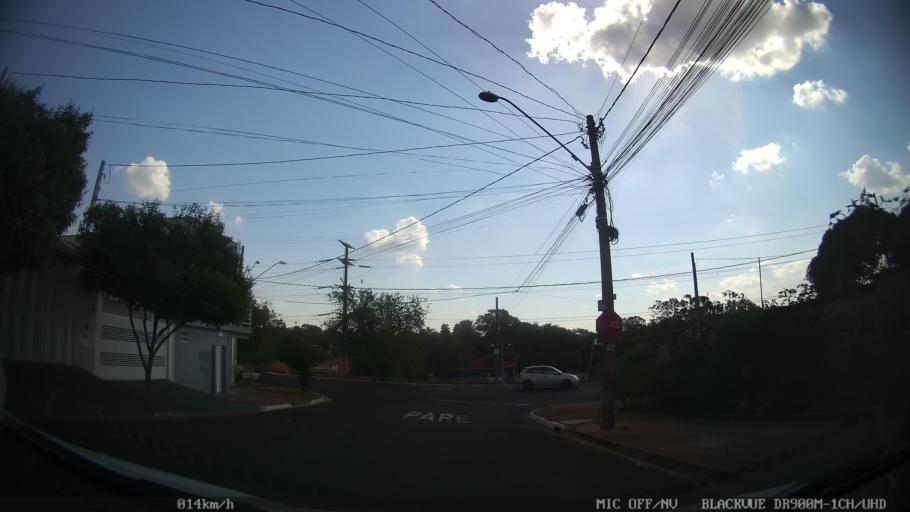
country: BR
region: Sao Paulo
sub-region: Ribeirao Preto
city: Ribeirao Preto
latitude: -21.1808
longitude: -47.8396
